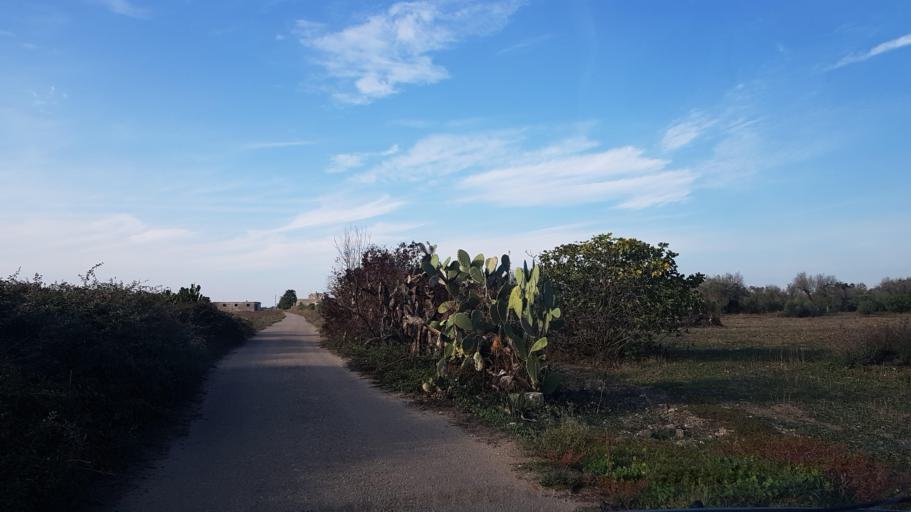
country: IT
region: Apulia
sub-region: Provincia di Brindisi
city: San Pancrazio Salentino
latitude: 40.4936
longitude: 17.8539
